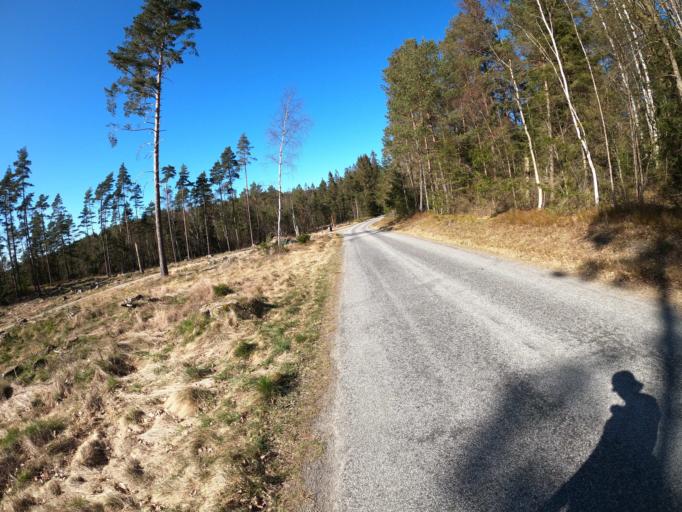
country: SE
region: Vaestra Goetaland
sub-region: Harryda Kommun
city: Molnlycke
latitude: 57.6369
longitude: 12.1137
